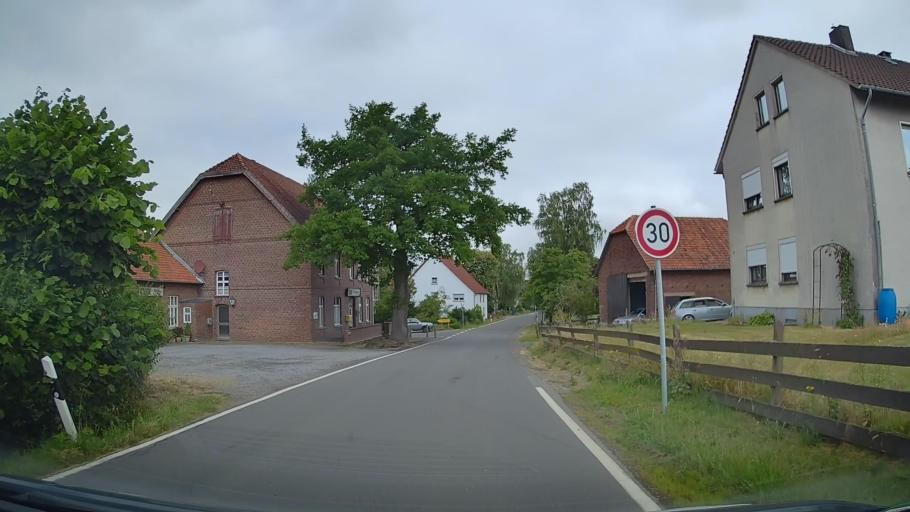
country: DE
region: Lower Saxony
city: Rinteln
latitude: 52.1007
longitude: 9.1225
